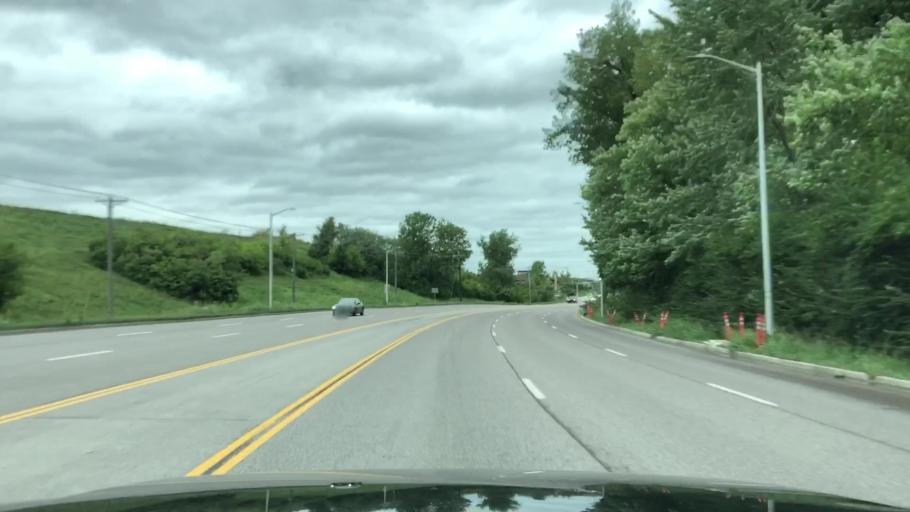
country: US
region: Missouri
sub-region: Saint Charles County
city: Saint Charles
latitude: 38.7463
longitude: -90.4645
